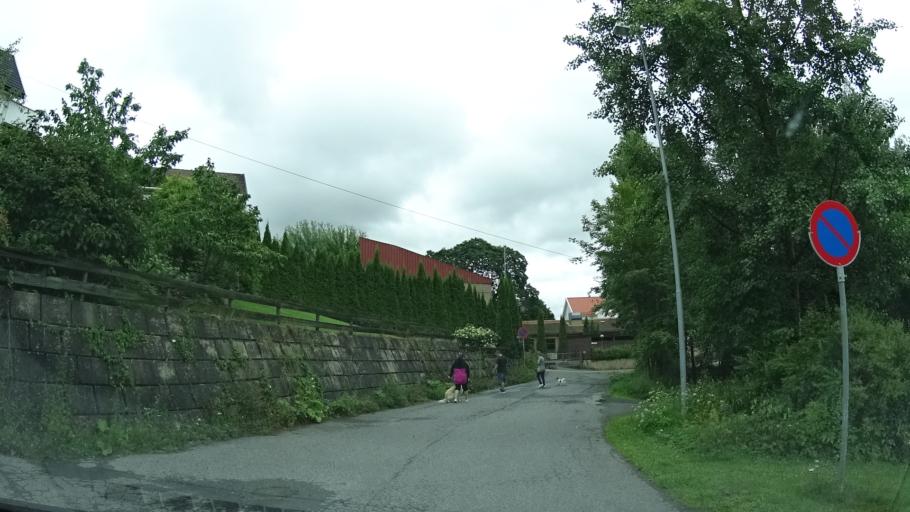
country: NO
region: Buskerud
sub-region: Ringerike
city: Honefoss
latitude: 60.1709
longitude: 10.2555
